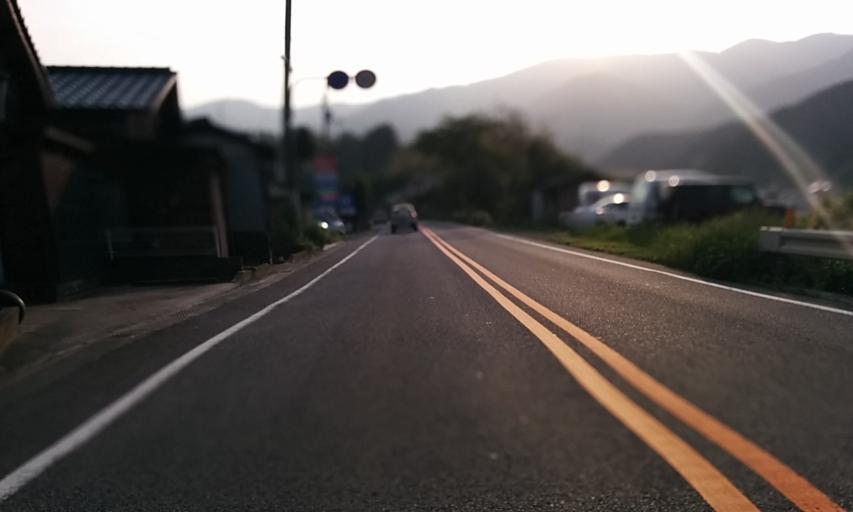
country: JP
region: Ehime
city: Saijo
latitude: 33.8563
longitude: 133.0153
